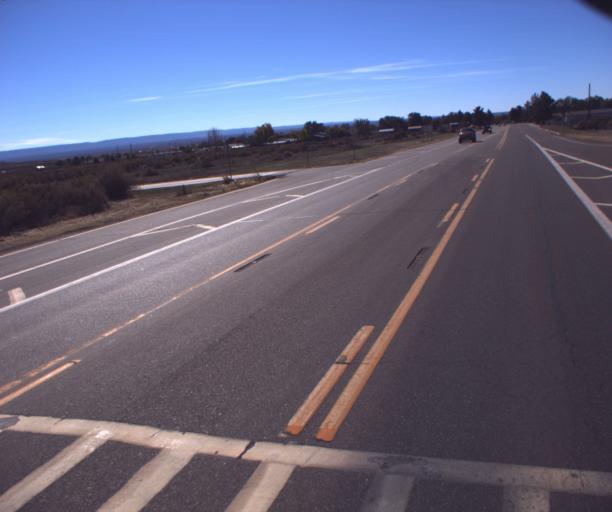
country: US
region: Arizona
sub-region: Coconino County
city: Fredonia
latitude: 36.9600
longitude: -112.5270
